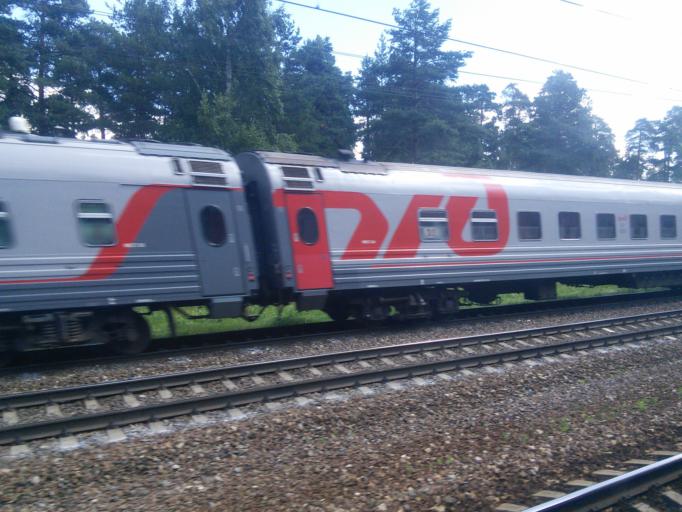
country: RU
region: Moskovskaya
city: Kratovo
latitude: 55.5797
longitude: 38.1903
